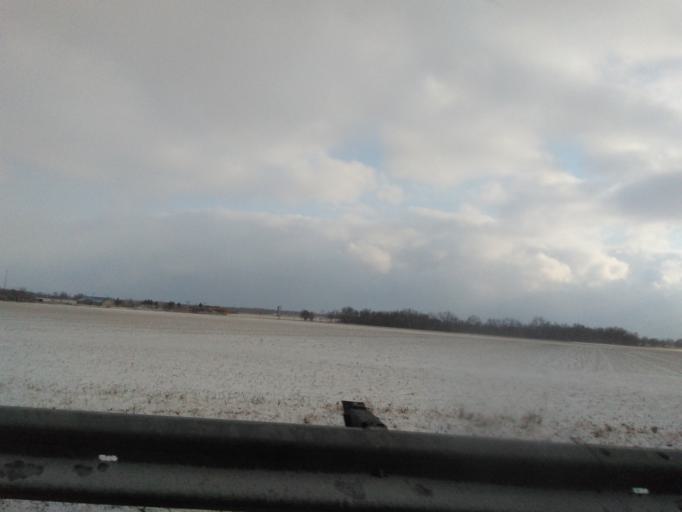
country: US
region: Illinois
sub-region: Bond County
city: Greenville
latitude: 38.8682
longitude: -89.4174
